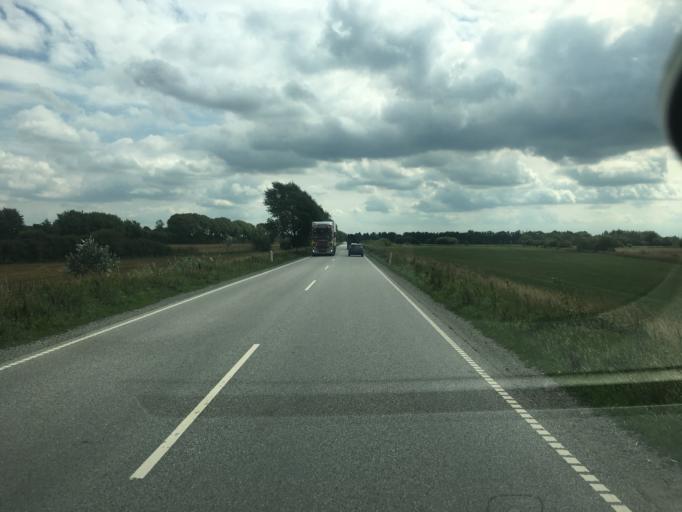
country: DK
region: South Denmark
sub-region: Aabenraa Kommune
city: Tinglev
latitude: 54.9802
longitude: 9.2947
